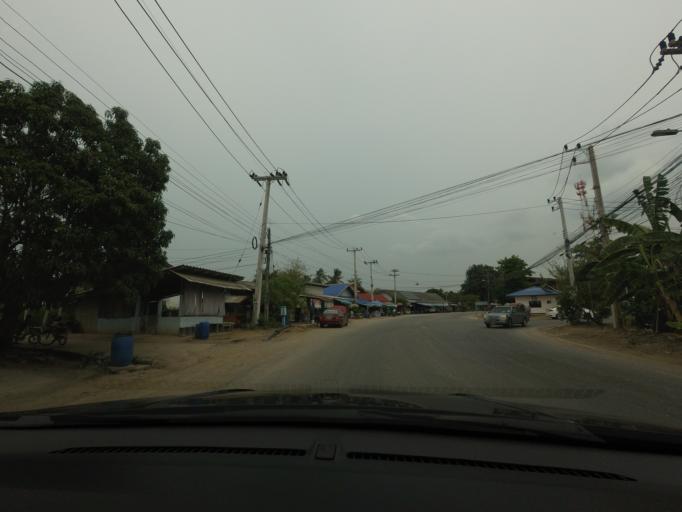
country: TH
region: Phetchaburi
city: Ban Laem
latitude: 13.1840
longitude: 99.9490
